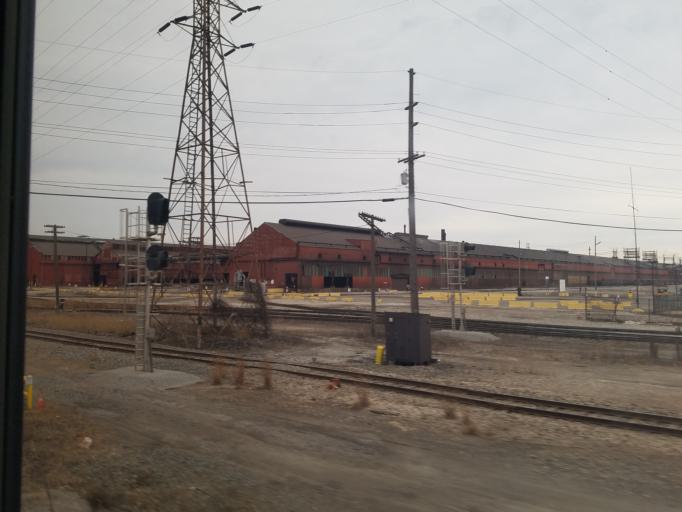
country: US
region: Indiana
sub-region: Lake County
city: East Chicago
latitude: 41.6536
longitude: -87.4426
